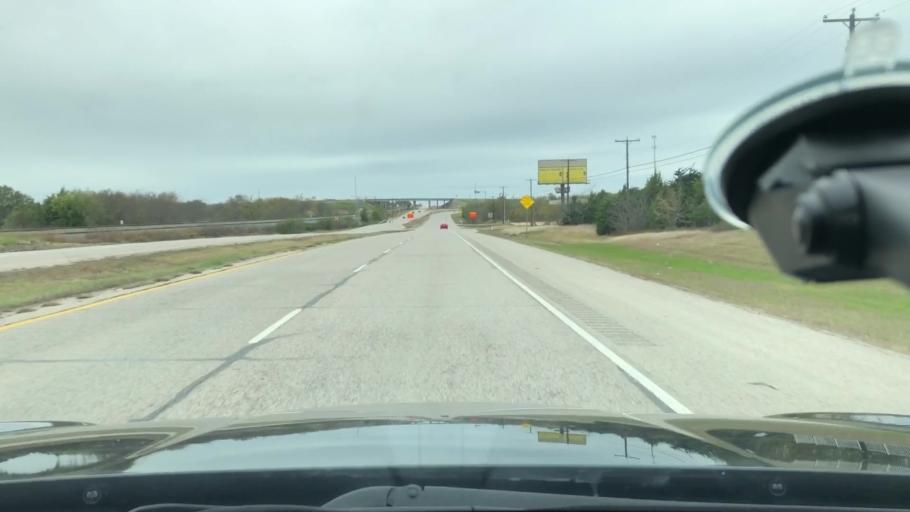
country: US
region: Texas
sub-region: Kaufman County
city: Talty
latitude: 32.7384
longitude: -96.3478
